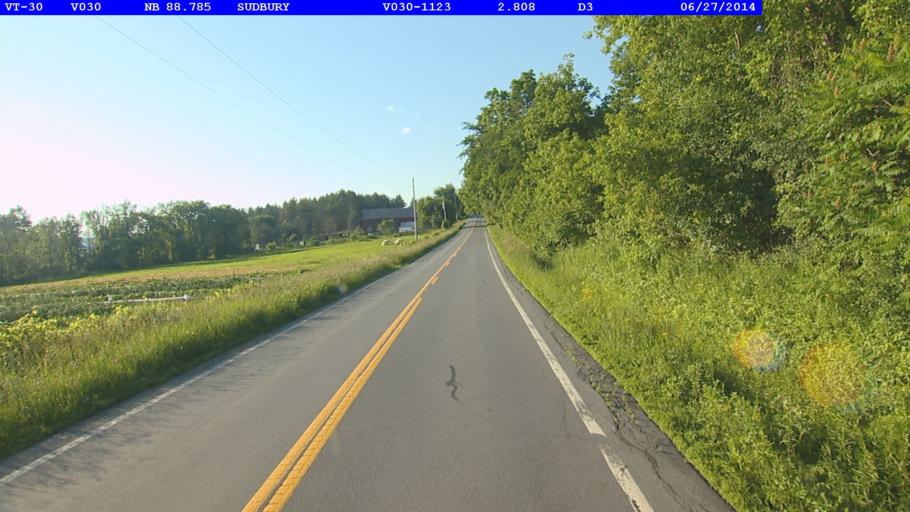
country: US
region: Vermont
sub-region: Rutland County
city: Brandon
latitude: 43.7885
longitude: -73.2037
